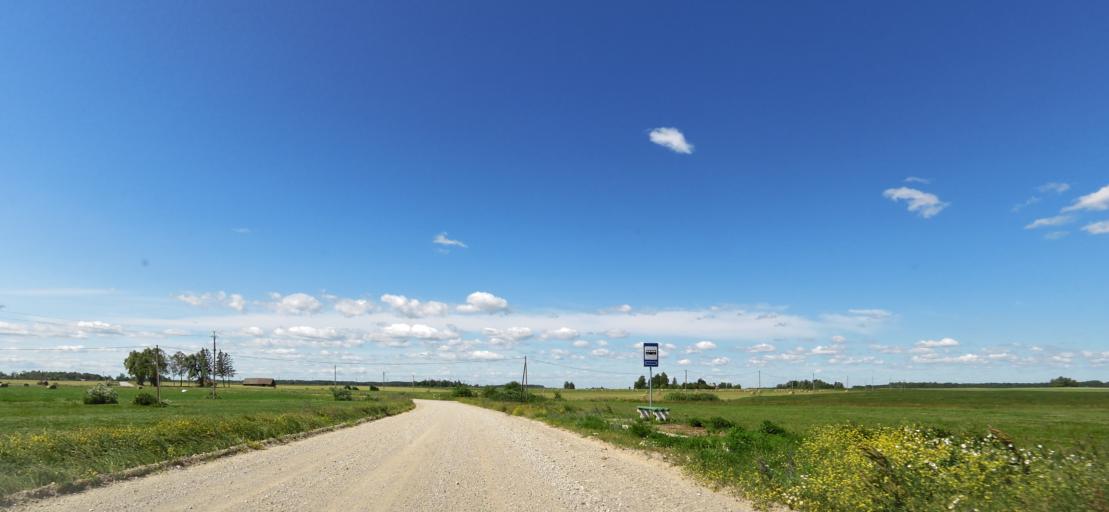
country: LT
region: Panevezys
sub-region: Birzai
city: Birzai
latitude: 56.2652
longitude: 24.5629
